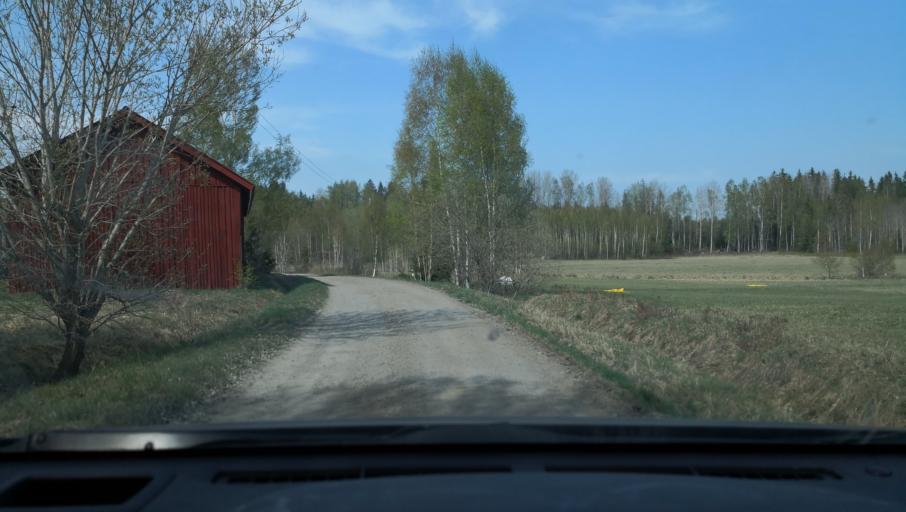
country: SE
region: Vaestmanland
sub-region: Vasteras
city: Skultuna
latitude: 59.8049
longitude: 16.4333
